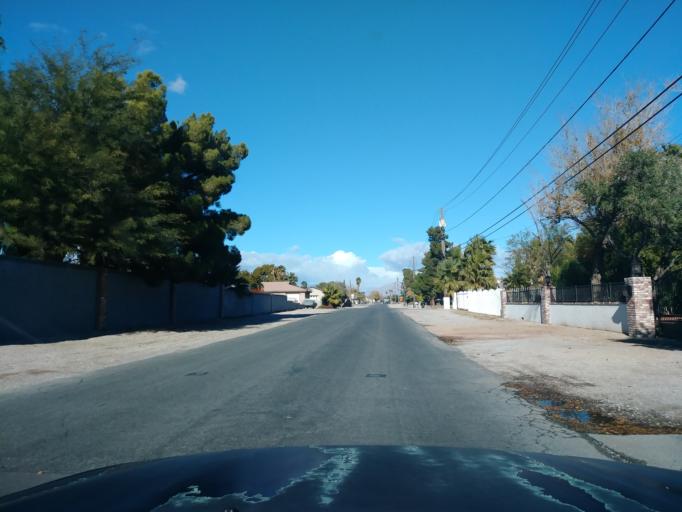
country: US
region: Nevada
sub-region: Clark County
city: Spring Valley
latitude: 36.1469
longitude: -115.2146
